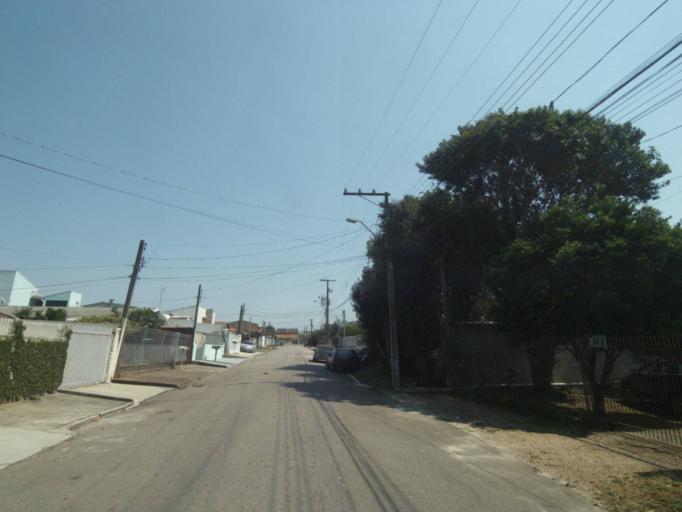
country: BR
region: Parana
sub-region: Sao Jose Dos Pinhais
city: Sao Jose dos Pinhais
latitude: -25.5142
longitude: -49.2789
